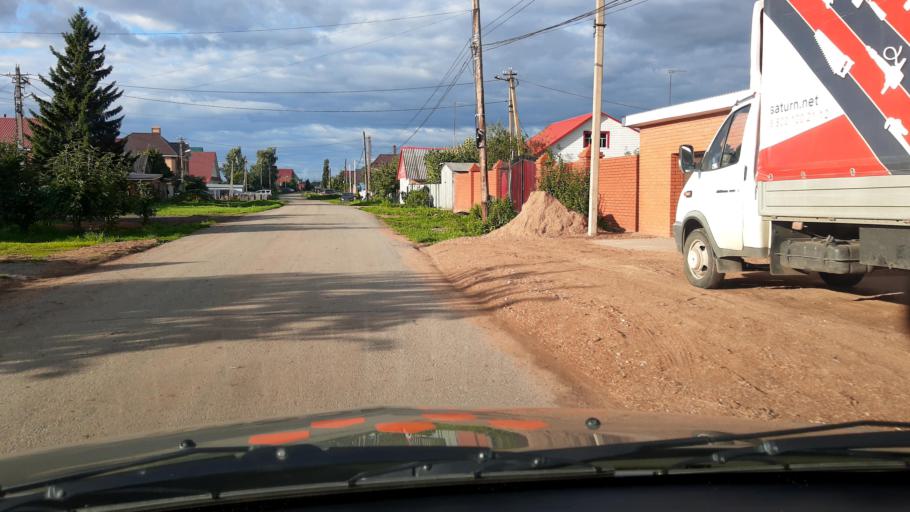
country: RU
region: Bashkortostan
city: Ufa
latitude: 54.8373
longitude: 56.0042
